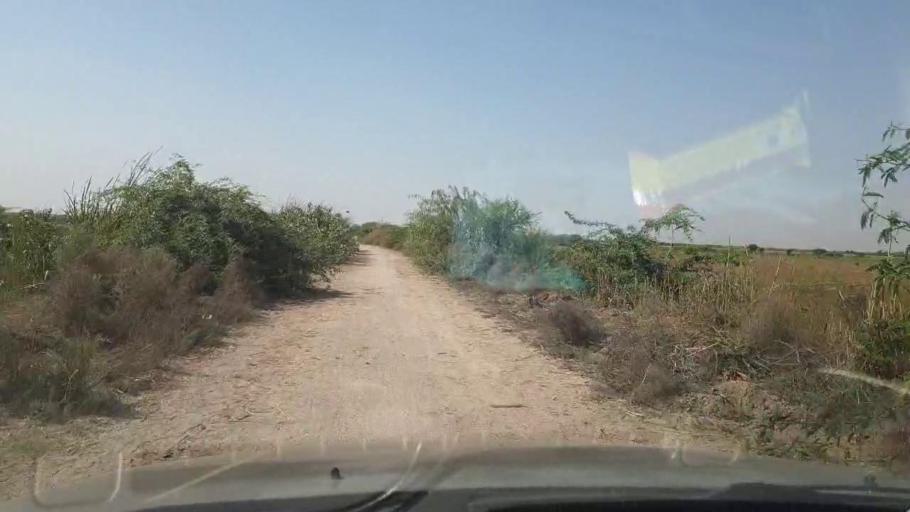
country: PK
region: Sindh
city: Daro Mehar
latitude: 24.9746
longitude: 68.1084
